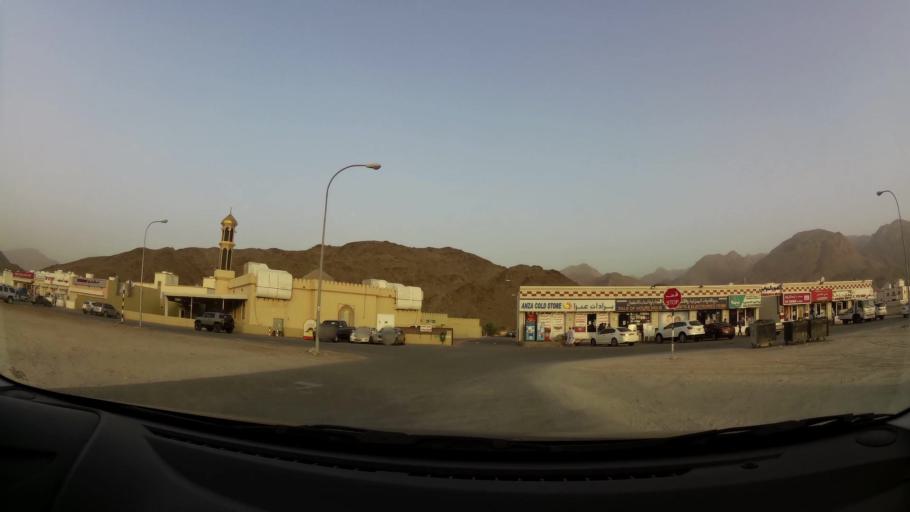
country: OM
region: Muhafazat Masqat
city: Bawshar
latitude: 23.4813
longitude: 58.3091
